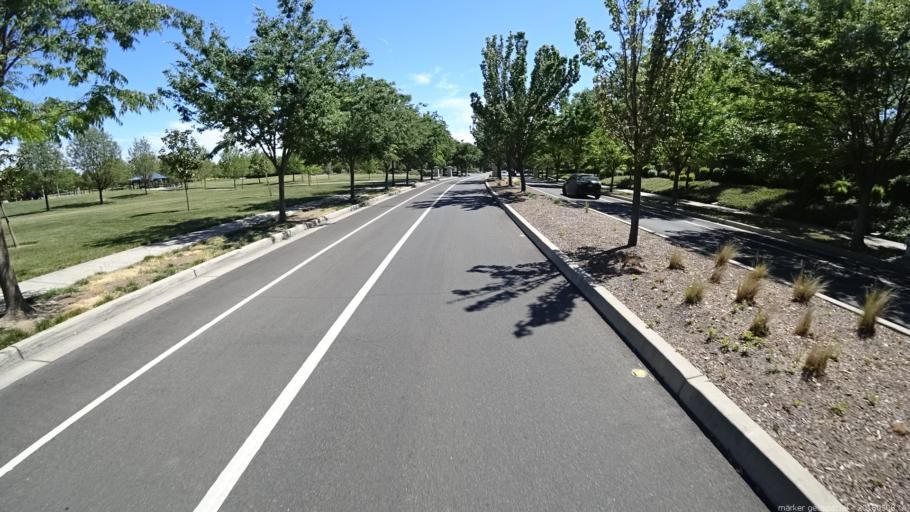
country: US
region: California
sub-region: Sacramento County
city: Elverta
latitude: 38.6741
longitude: -121.5191
